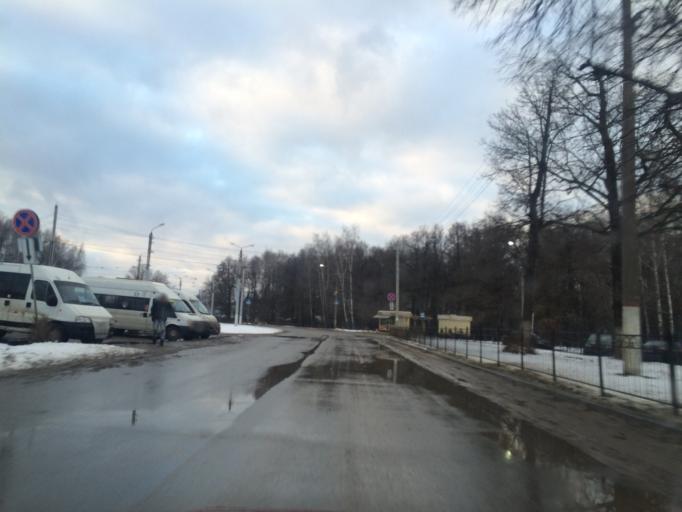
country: RU
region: Tula
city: Tula
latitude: 54.2185
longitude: 37.7076
